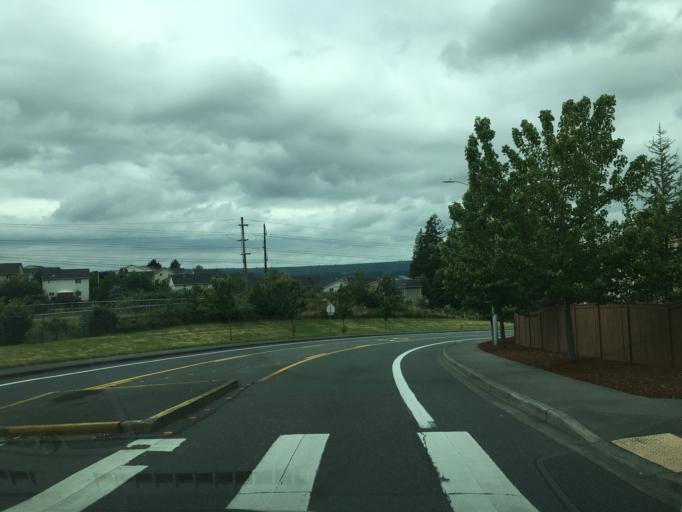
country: US
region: Washington
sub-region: Snohomish County
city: Sisco Heights
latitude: 48.0721
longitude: -122.1212
